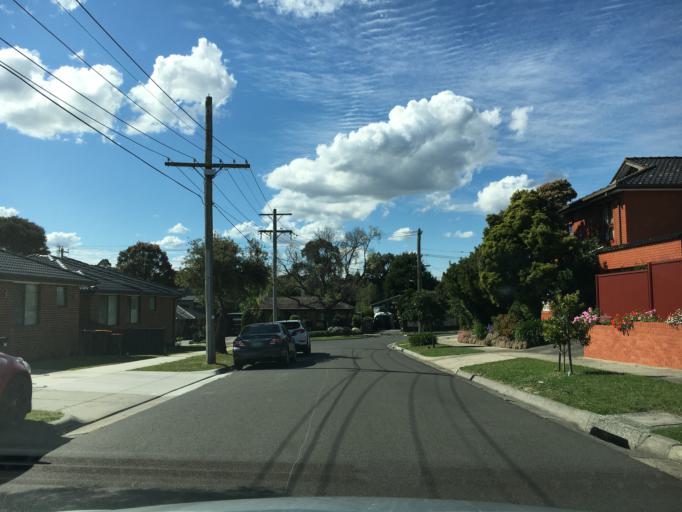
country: AU
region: Victoria
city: Clayton
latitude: -37.8931
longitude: 145.1214
